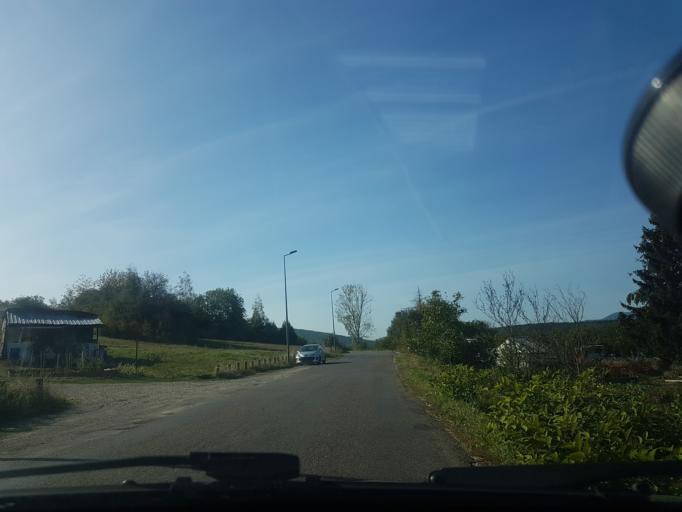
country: FR
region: Franche-Comte
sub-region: Territoire de Belfort
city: Offemont
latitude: 47.6507
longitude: 6.8768
